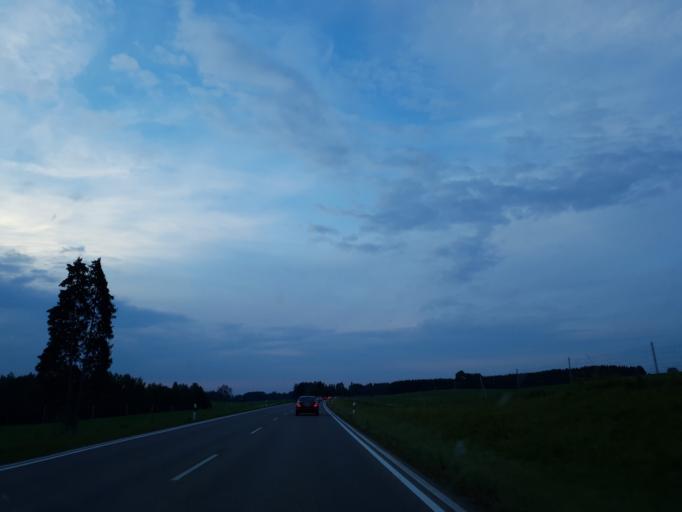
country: DE
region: Bavaria
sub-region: Swabia
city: Mauerstetten
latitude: 47.8578
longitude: 10.6598
